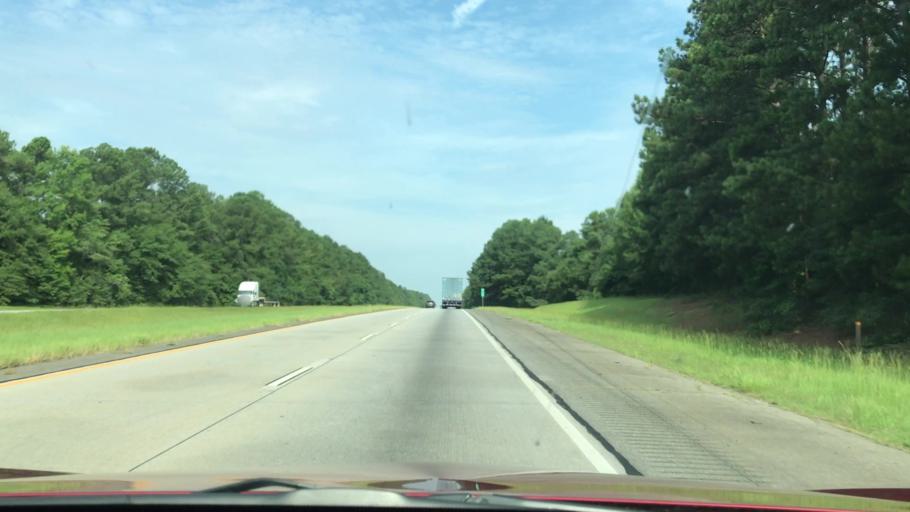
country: US
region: Georgia
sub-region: Warren County
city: Firing Range
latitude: 33.4965
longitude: -82.6884
